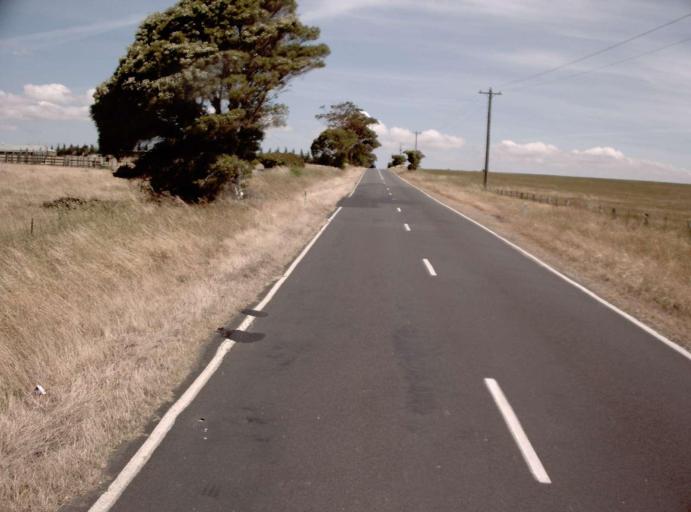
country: AU
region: Victoria
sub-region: Wellington
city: Heyfield
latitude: -38.1115
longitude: 146.8620
